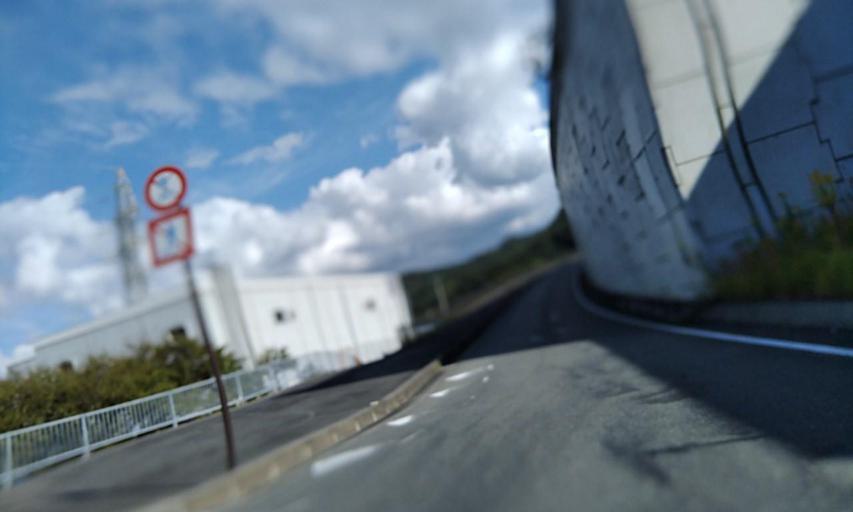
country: JP
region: Wakayama
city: Tanabe
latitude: 33.7518
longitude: 135.3529
